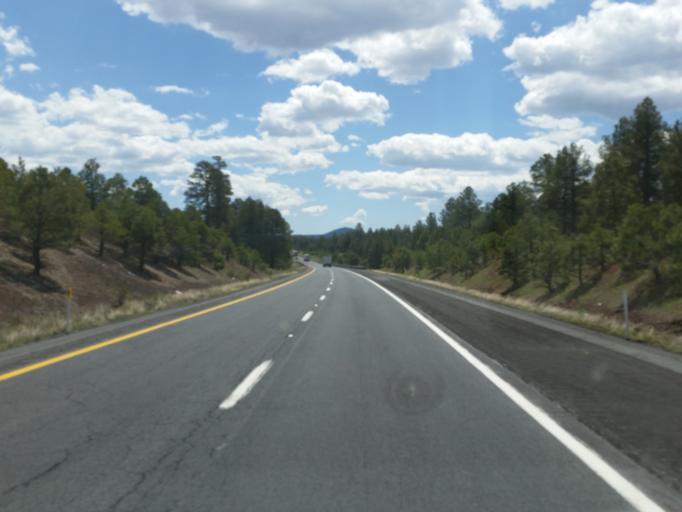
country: US
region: Arizona
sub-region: Coconino County
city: Parks
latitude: 35.2496
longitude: -111.9922
